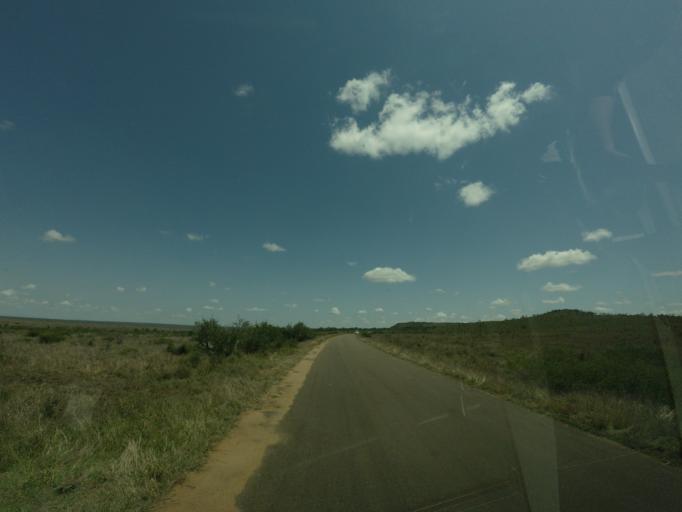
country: ZA
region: Mpumalanga
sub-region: Ehlanzeni District
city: Komatipoort
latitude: -24.8859
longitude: 31.9025
